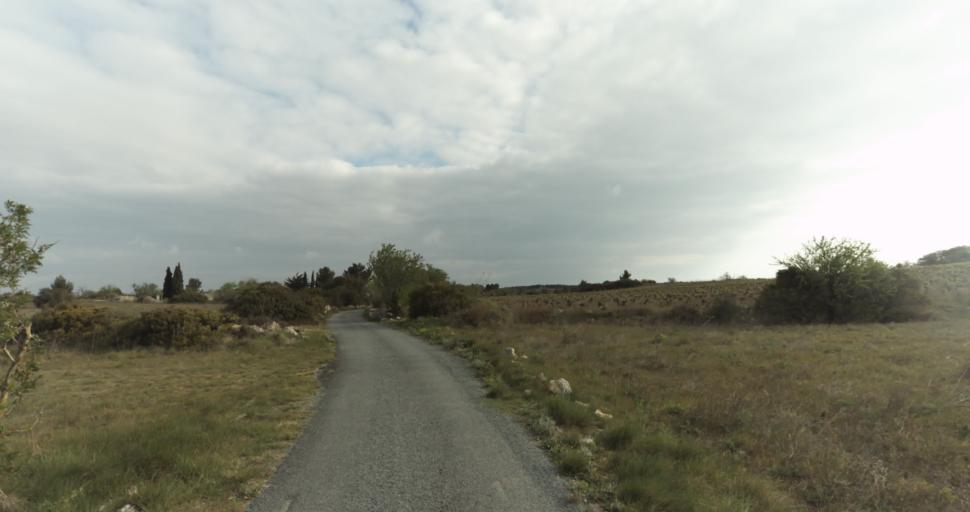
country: FR
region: Languedoc-Roussillon
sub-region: Departement de l'Aude
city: Leucate
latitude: 42.9219
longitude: 3.0259
